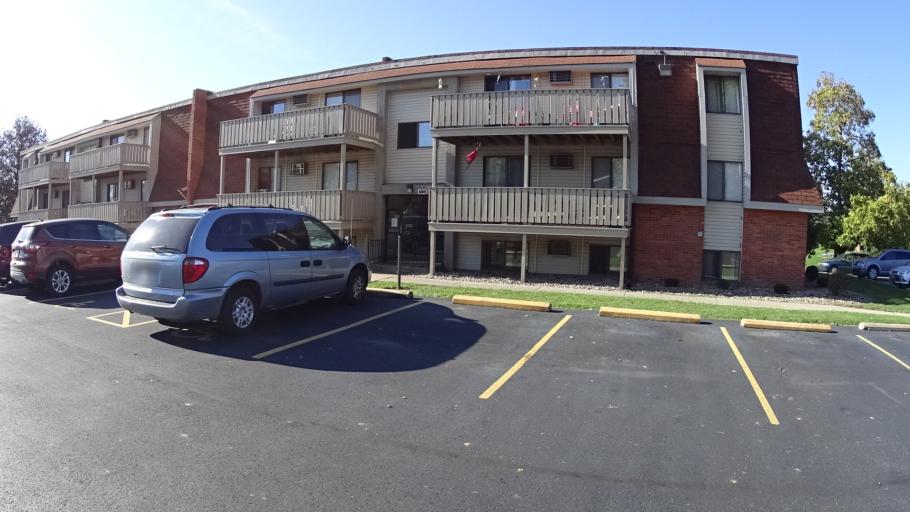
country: US
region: Ohio
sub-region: Lorain County
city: Vermilion
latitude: 41.4265
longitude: -82.3482
